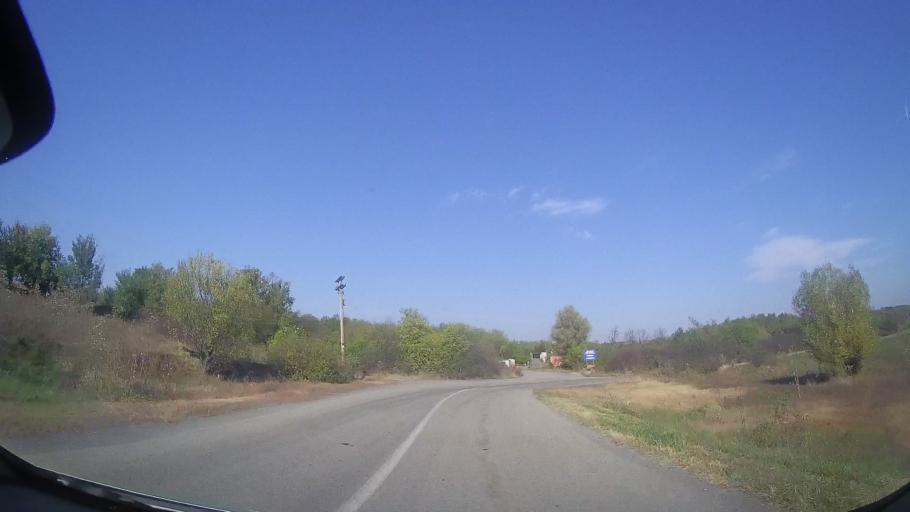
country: RO
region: Timis
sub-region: Comuna Ghizela
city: Ghizela
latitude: 45.8077
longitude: 21.7206
